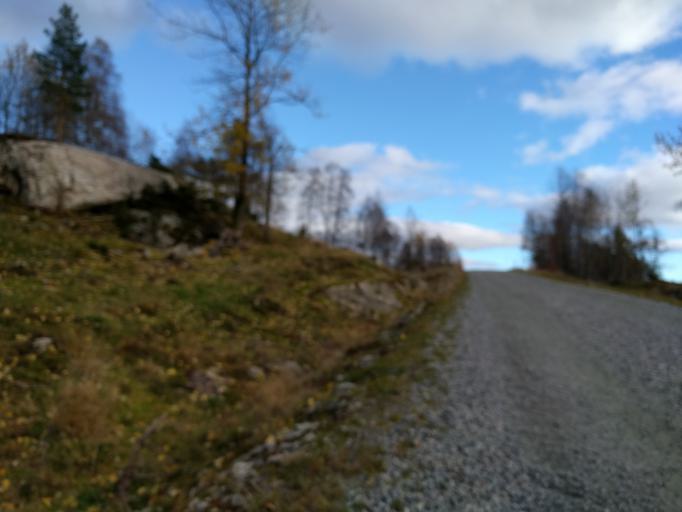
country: NO
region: Aust-Agder
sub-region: Evje og Hornnes
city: Evje
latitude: 58.6531
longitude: 7.9472
